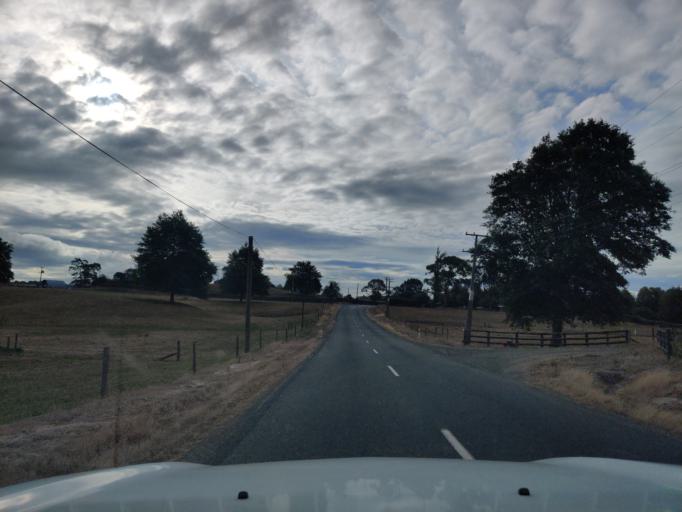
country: NZ
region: Waikato
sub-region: Waipa District
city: Cambridge
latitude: -37.7936
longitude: 175.4330
